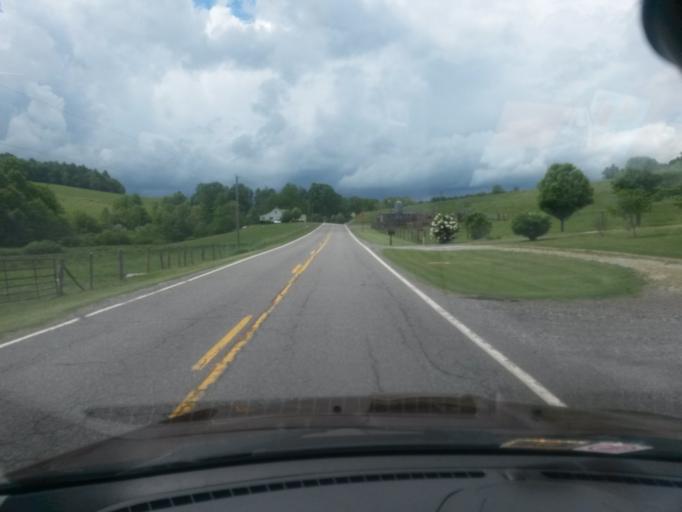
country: US
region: Virginia
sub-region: Floyd County
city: Floyd
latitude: 36.8561
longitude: -80.3210
